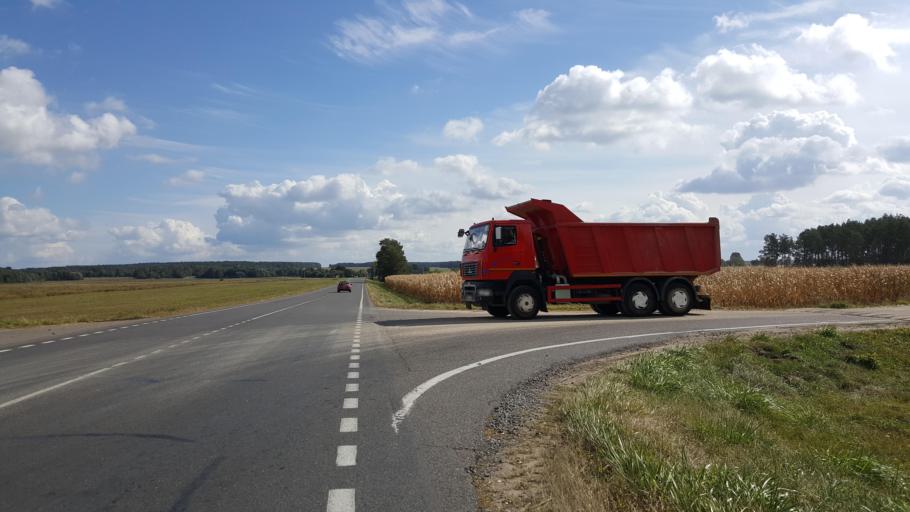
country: BY
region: Brest
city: Kamyanyets
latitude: 52.4007
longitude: 23.8774
